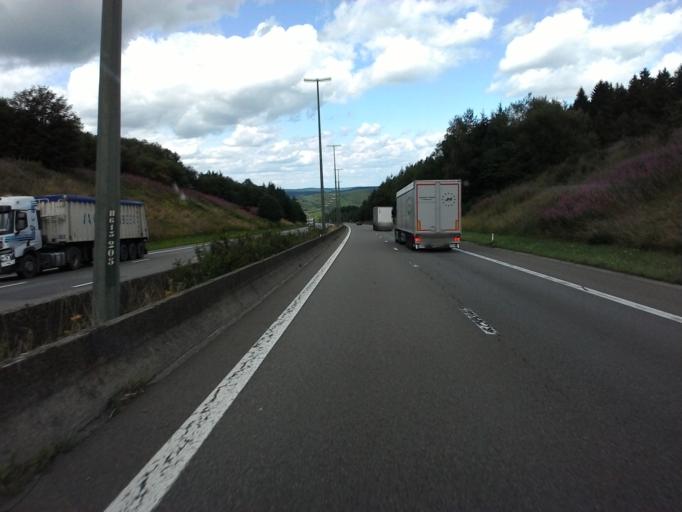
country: BE
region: Wallonia
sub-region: Province du Luxembourg
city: Manhay
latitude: 50.2831
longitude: 5.7281
